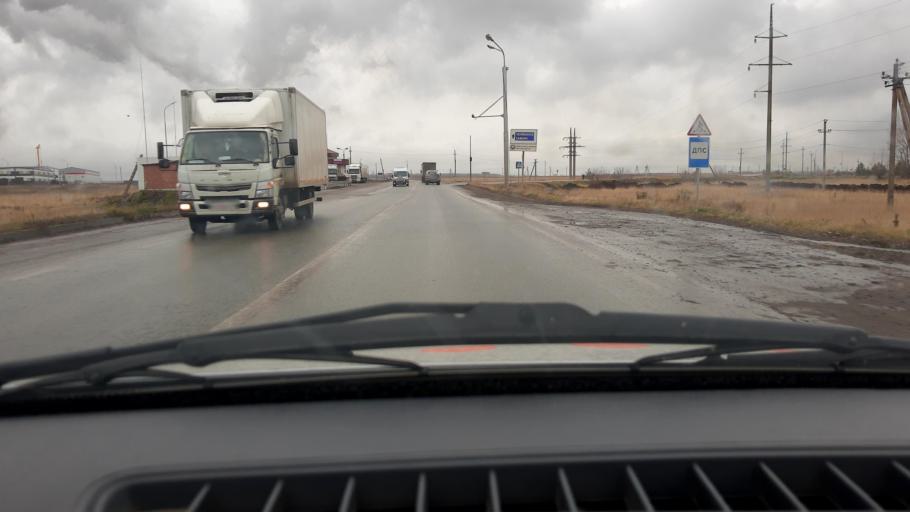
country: RU
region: Bashkortostan
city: Iglino
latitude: 54.7676
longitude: 56.2617
